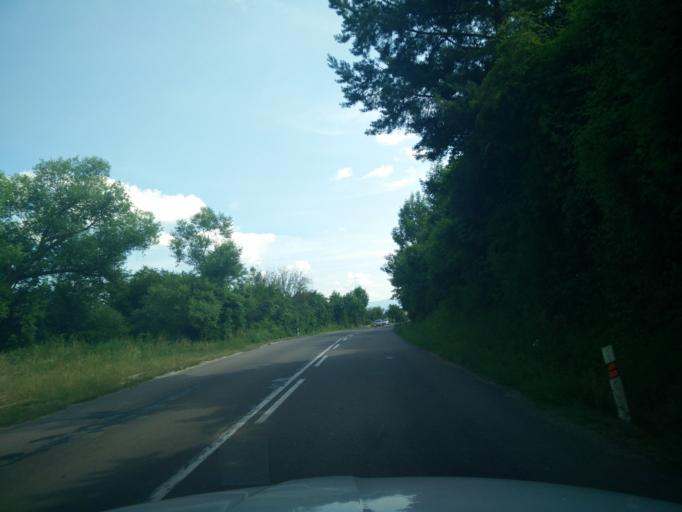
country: SK
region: Nitriansky
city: Prievidza
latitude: 48.8852
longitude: 18.6381
